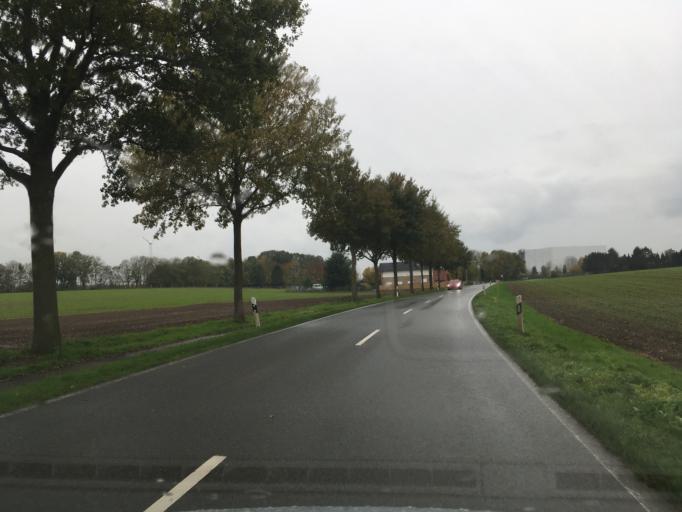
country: DE
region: North Rhine-Westphalia
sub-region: Regierungsbezirk Munster
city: Klein Reken
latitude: 51.8073
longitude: 7.0642
